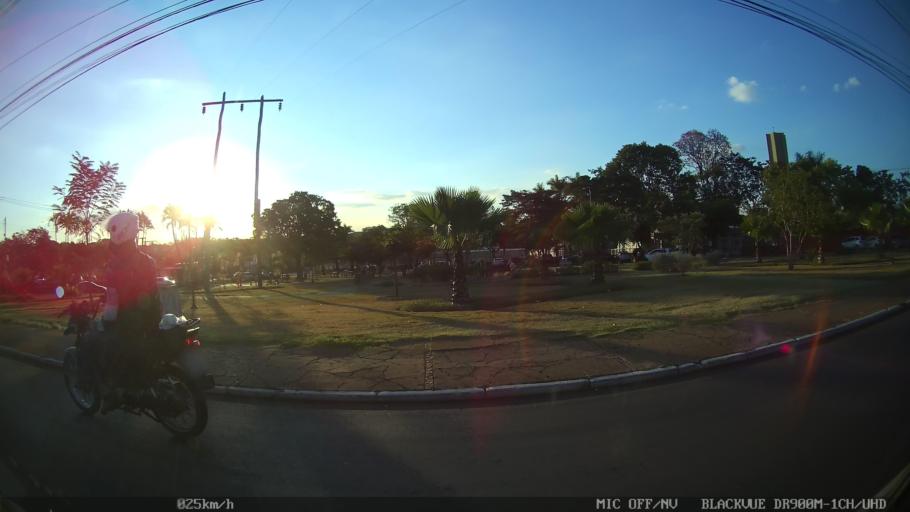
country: BR
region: Sao Paulo
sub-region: Santa Barbara D'Oeste
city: Santa Barbara d'Oeste
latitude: -22.7429
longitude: -47.4078
